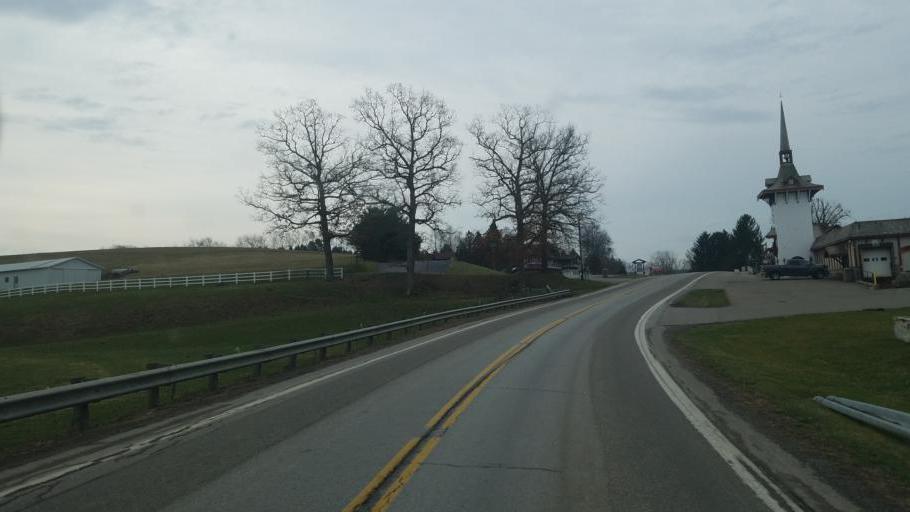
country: US
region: Ohio
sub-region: Holmes County
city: Millersburg
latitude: 40.5260
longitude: -81.8052
